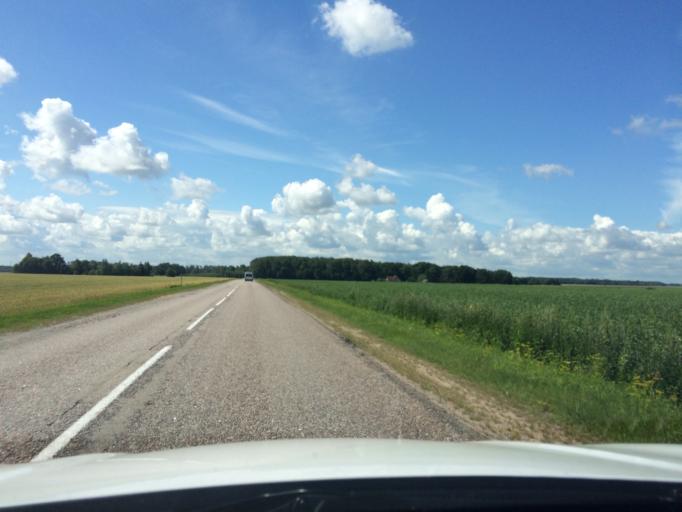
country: LV
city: Tervete
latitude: 56.5238
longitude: 23.4995
